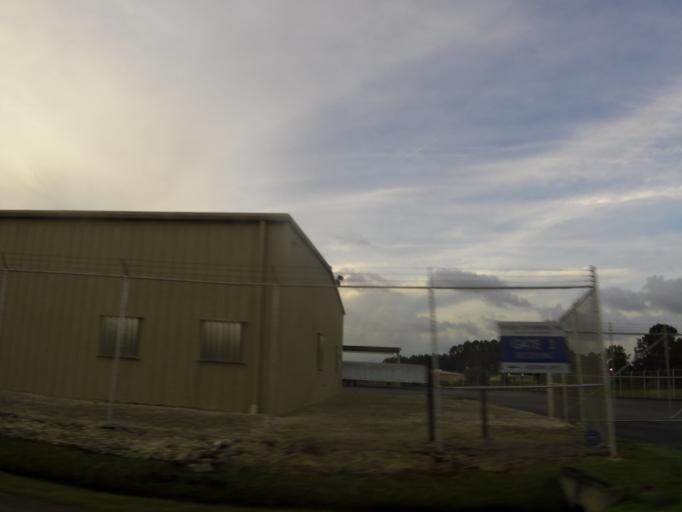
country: US
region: Florida
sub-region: Duval County
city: Jacksonville
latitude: 30.3632
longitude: -81.7130
